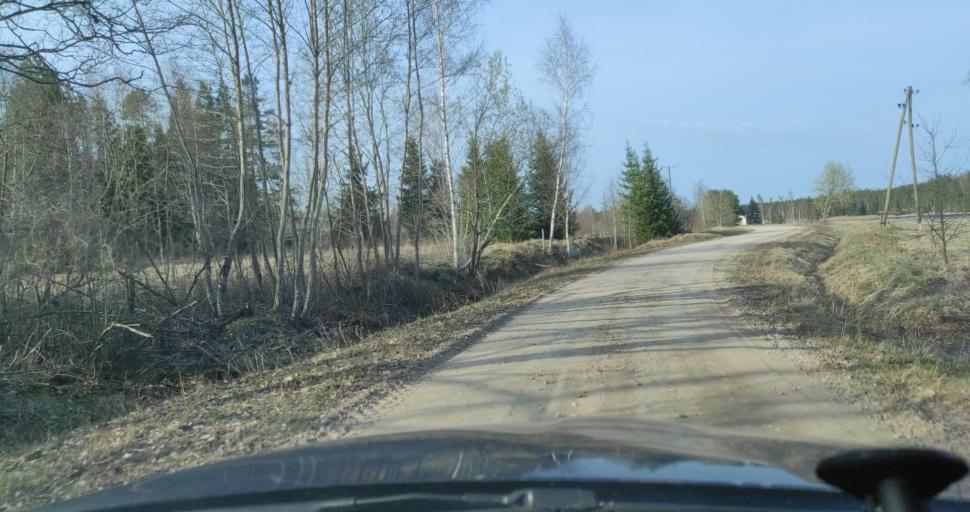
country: LV
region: Kuldigas Rajons
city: Kuldiga
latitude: 57.0055
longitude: 22.0136
